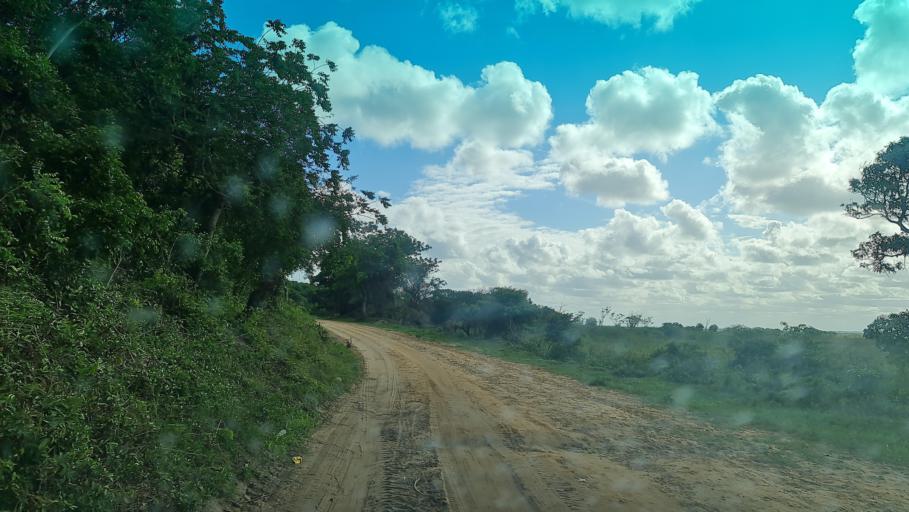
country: MZ
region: Maputo
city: Manhica
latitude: -25.4349
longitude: 32.8841
